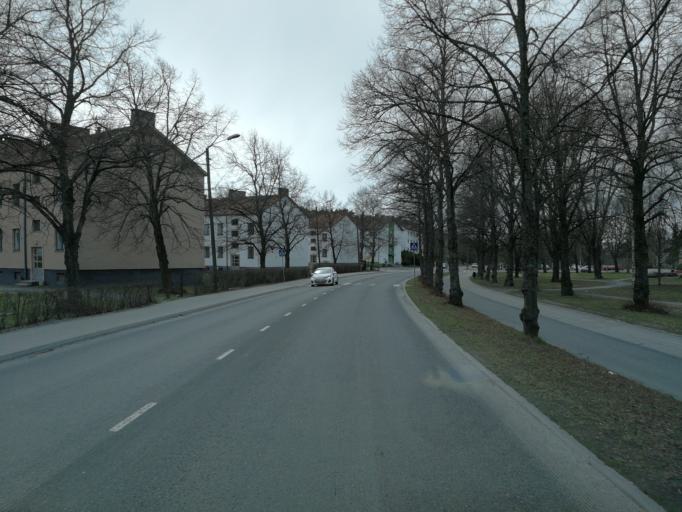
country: FI
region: Varsinais-Suomi
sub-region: Turku
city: Turku
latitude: 60.4386
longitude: 22.2698
